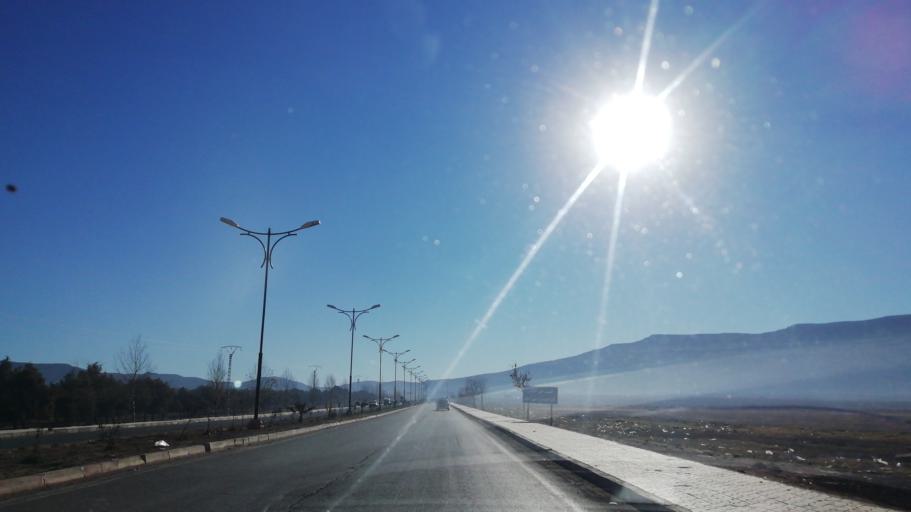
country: DZ
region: El Bayadh
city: El Bayadh
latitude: 33.6648
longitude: 1.0495
